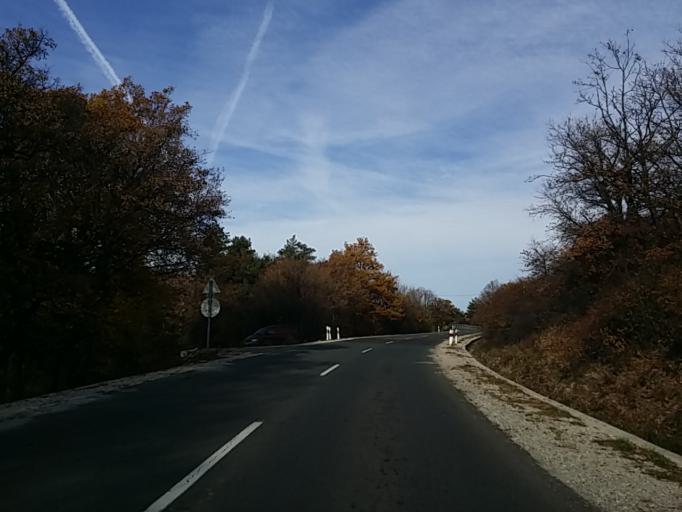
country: HU
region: Heves
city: Gyongyossolymos
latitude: 47.8453
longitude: 19.9579
